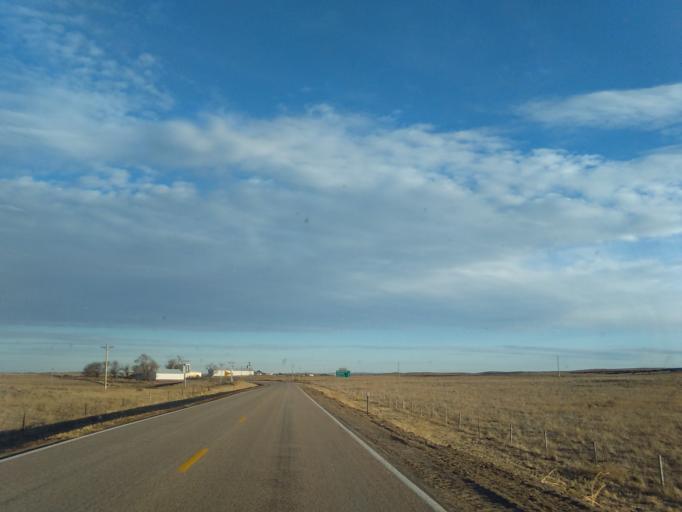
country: US
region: Nebraska
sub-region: Morrill County
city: Bridgeport
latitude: 41.6001
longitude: -102.9800
